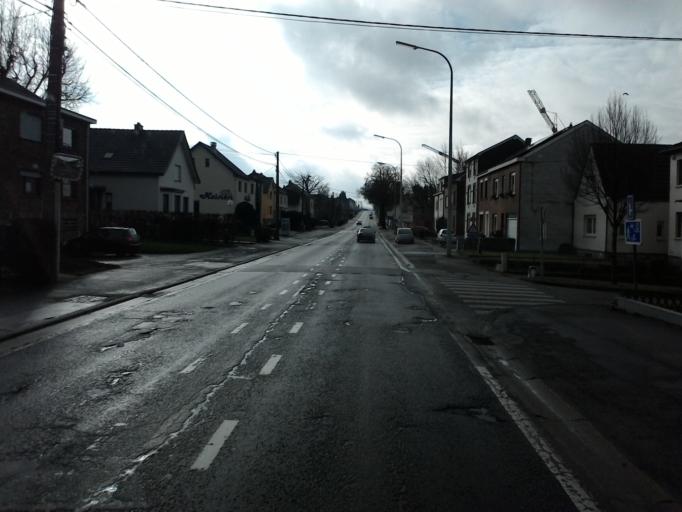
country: BE
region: Wallonia
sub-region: Province de Liege
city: Eupen
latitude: 50.6434
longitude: 6.0445
